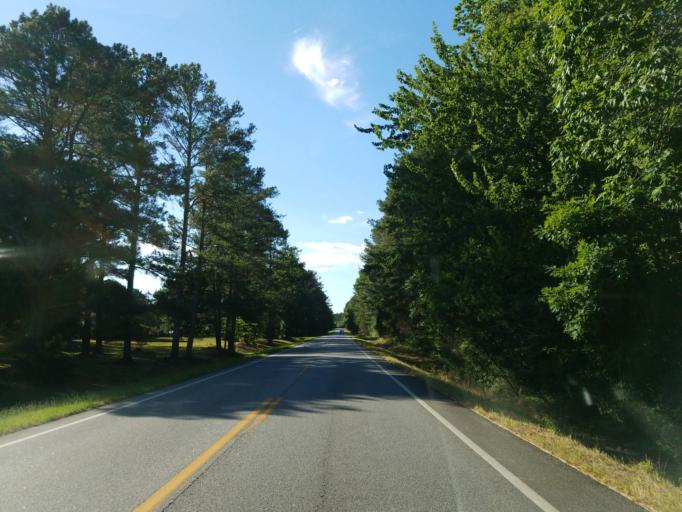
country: US
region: Georgia
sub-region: Gordon County
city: Calhoun
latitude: 34.6006
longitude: -85.0361
